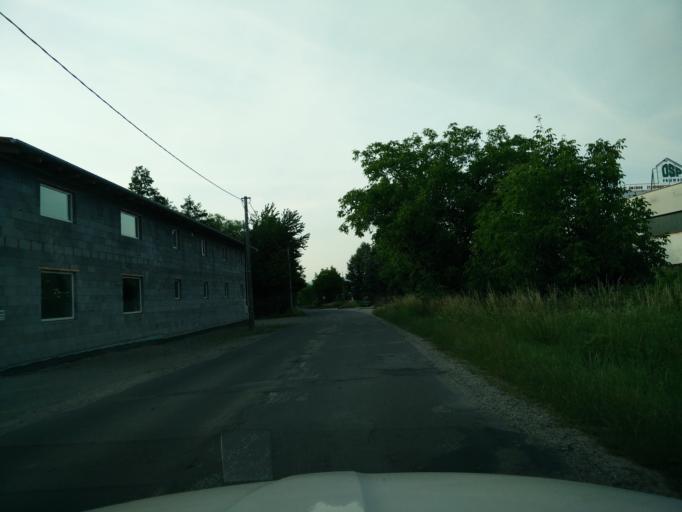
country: SK
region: Nitriansky
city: Prievidza
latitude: 48.7494
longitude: 18.6242
